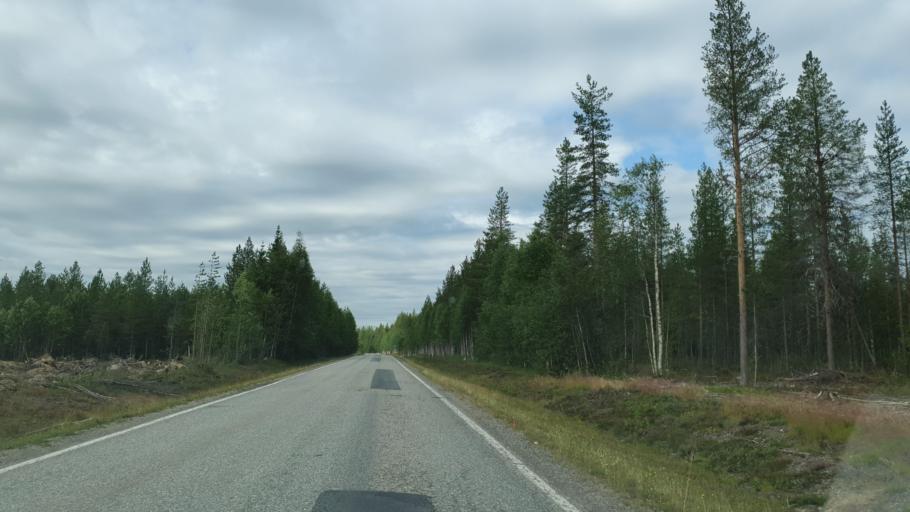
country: FI
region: Lapland
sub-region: Tunturi-Lappi
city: Kittilae
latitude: 67.6159
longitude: 25.3439
